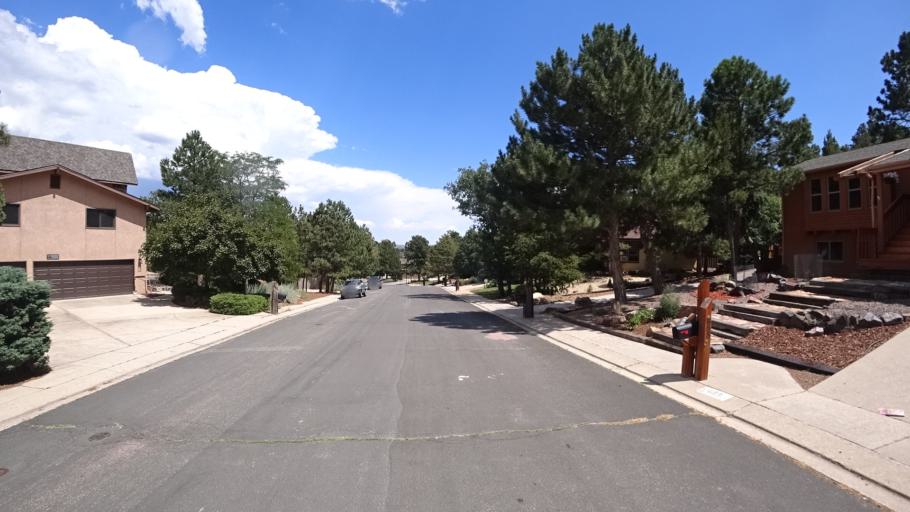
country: US
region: Colorado
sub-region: El Paso County
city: Air Force Academy
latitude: 38.9352
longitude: -104.8405
